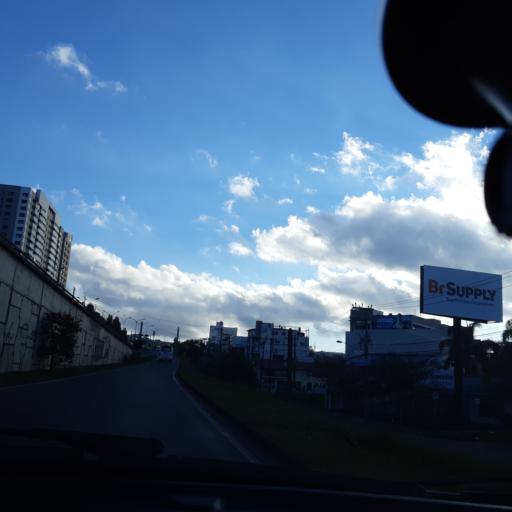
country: BR
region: Rio Grande do Sul
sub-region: Caxias Do Sul
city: Caxias do Sul
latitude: -29.1748
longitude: -51.2085
